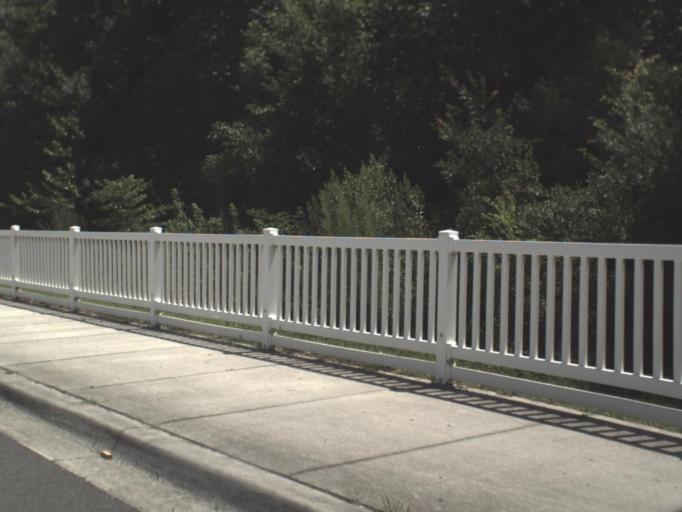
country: US
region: Florida
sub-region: Saint Johns County
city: Fruit Cove
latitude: 30.1029
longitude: -81.6270
